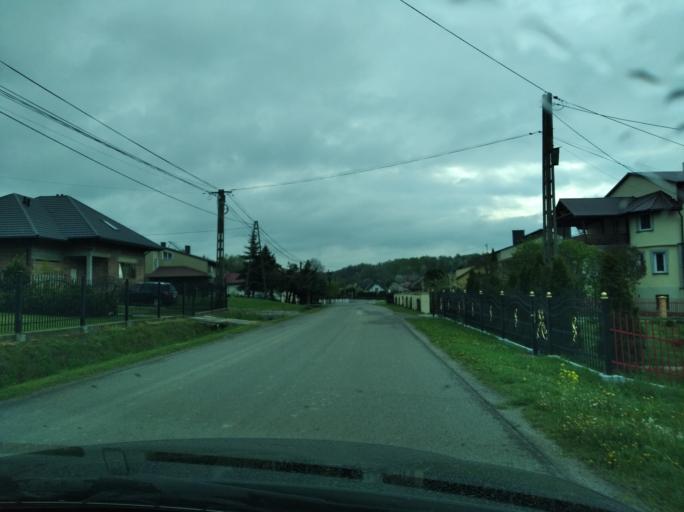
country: PL
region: Subcarpathian Voivodeship
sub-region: Powiat rzeszowski
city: Lecka
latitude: 49.8705
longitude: 22.0307
